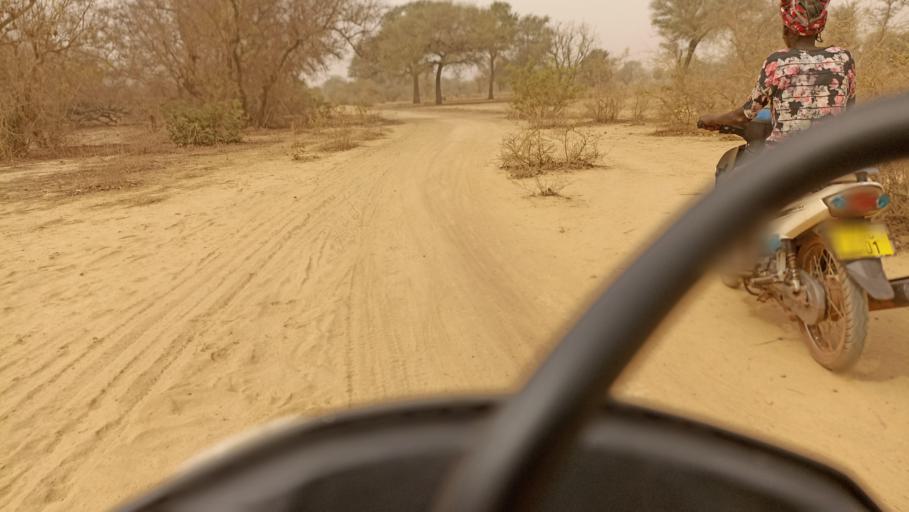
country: BF
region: Nord
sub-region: Province du Zondoma
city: Gourcy
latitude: 13.2782
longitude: -2.5346
